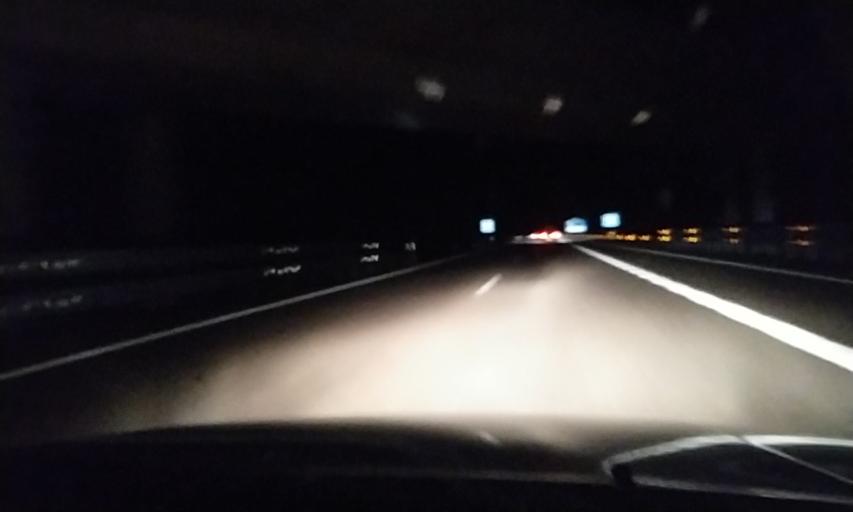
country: ES
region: Castille and Leon
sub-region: Provincia de Zamora
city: Pobladura del Valle
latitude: 42.1158
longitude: -5.7420
